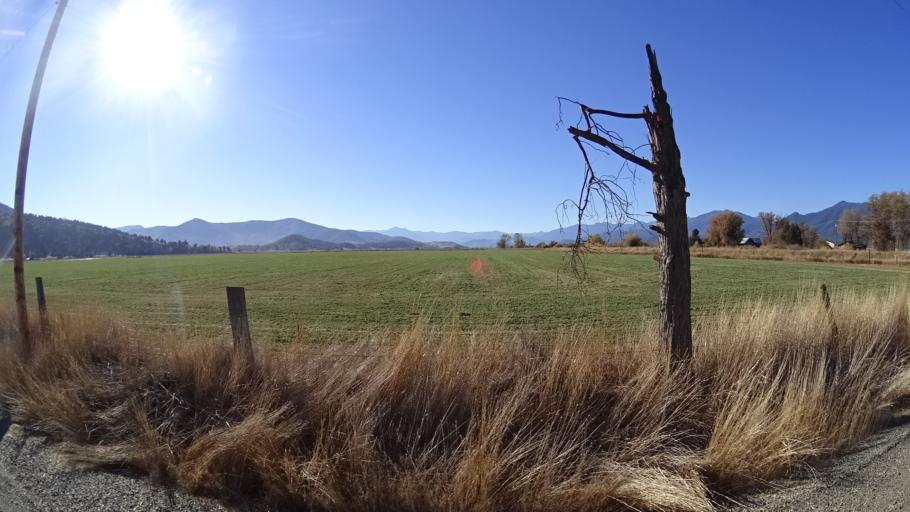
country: US
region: California
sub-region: Siskiyou County
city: Yreka
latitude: 41.5197
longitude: -122.8494
